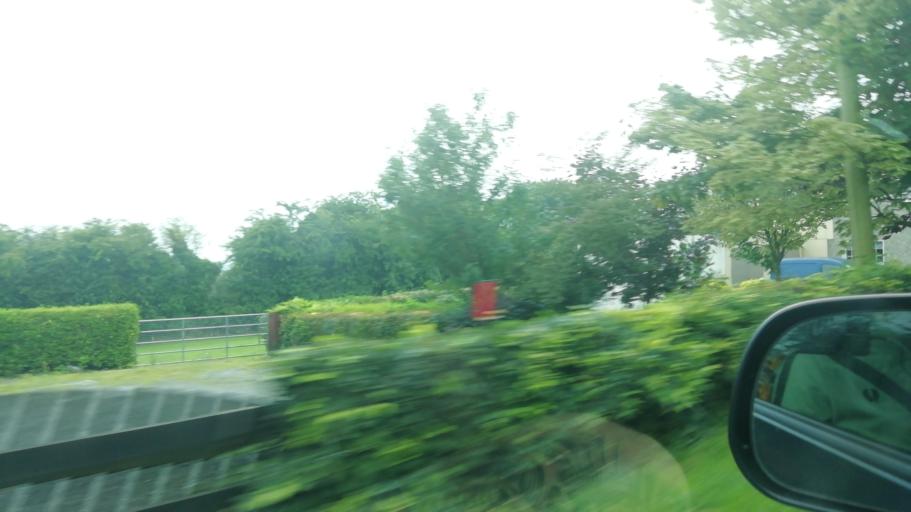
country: IE
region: Munster
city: Fethard
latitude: 52.5556
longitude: -7.6701
